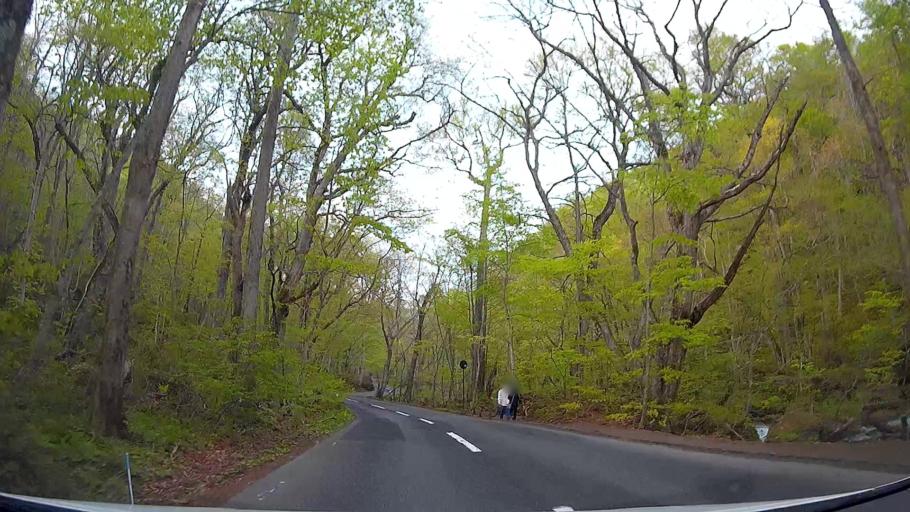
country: JP
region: Aomori
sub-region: Aomori Shi
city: Furudate
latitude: 40.5244
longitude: 140.9741
